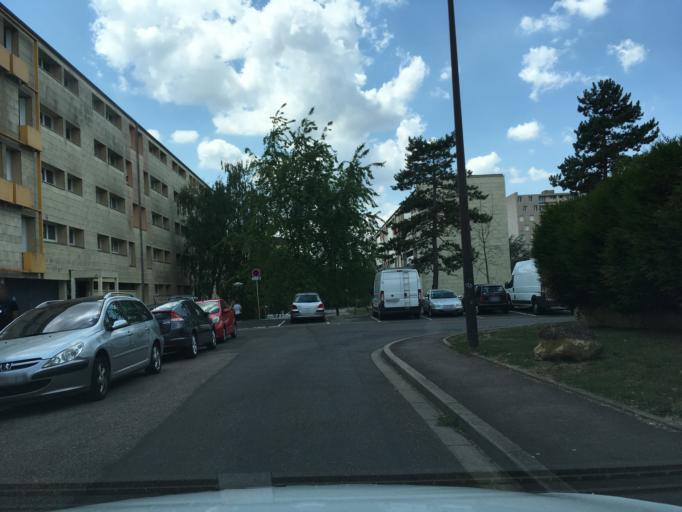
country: FR
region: Lorraine
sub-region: Departement de la Moselle
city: Saint-Julien-les-Metz
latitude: 49.1194
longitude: 6.1998
